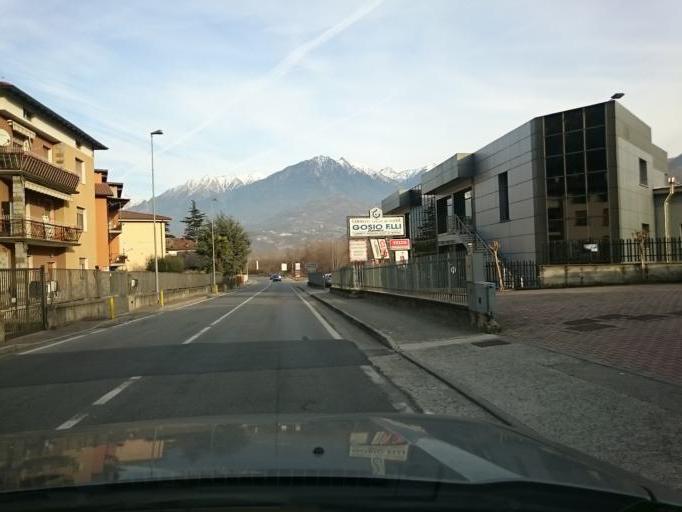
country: IT
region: Lombardy
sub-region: Provincia di Brescia
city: Esine
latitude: 45.9360
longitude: 10.2470
